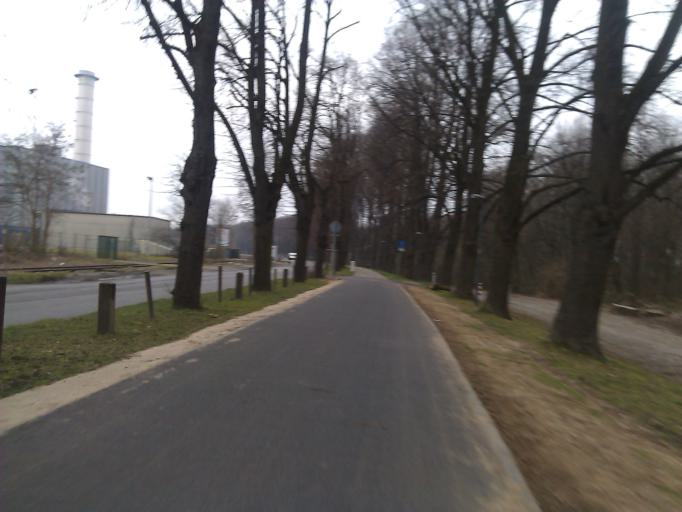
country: DE
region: North Rhine-Westphalia
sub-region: Regierungsbezirk Koln
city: Muelheim
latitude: 50.9732
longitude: 6.9917
